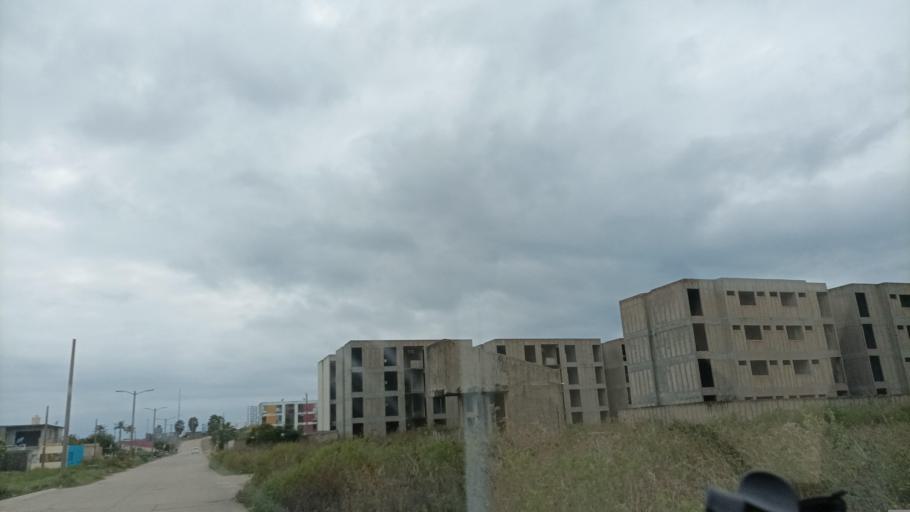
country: MX
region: Veracruz
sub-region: Coatzacoalcos
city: Fraccionamiento Ciudad Olmeca
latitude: 18.1577
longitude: -94.5579
